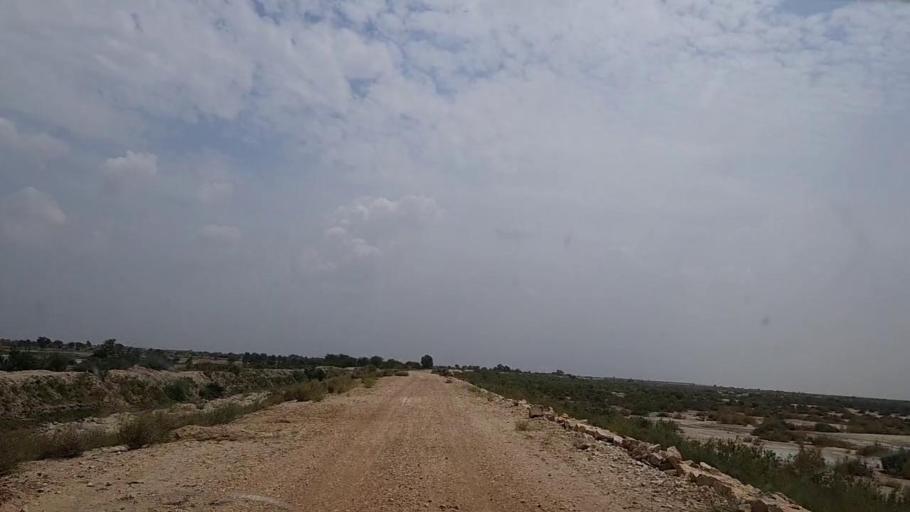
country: PK
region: Sindh
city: Phulji
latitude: 26.8342
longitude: 67.6175
